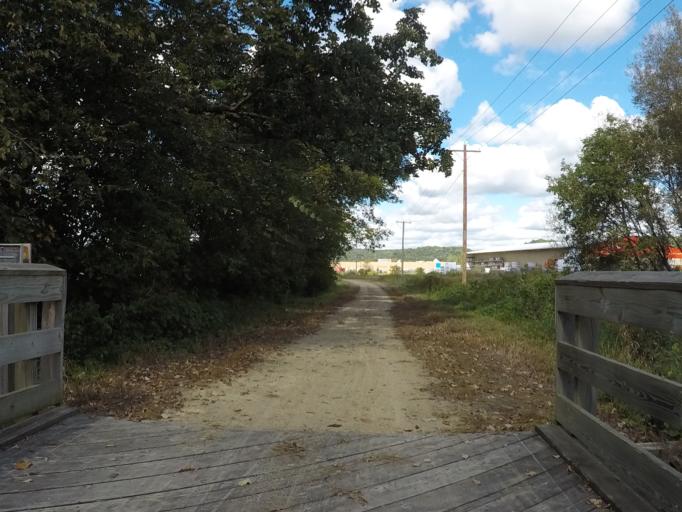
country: US
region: Wisconsin
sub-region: Richland County
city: Richland Center
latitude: 43.3094
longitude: -90.3453
